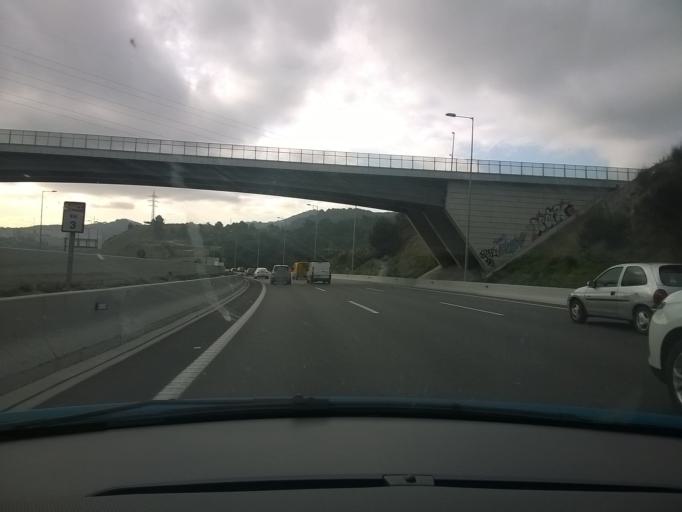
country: ES
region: Catalonia
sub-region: Provincia de Barcelona
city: Montcada i Reixac
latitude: 41.4729
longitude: 2.1631
